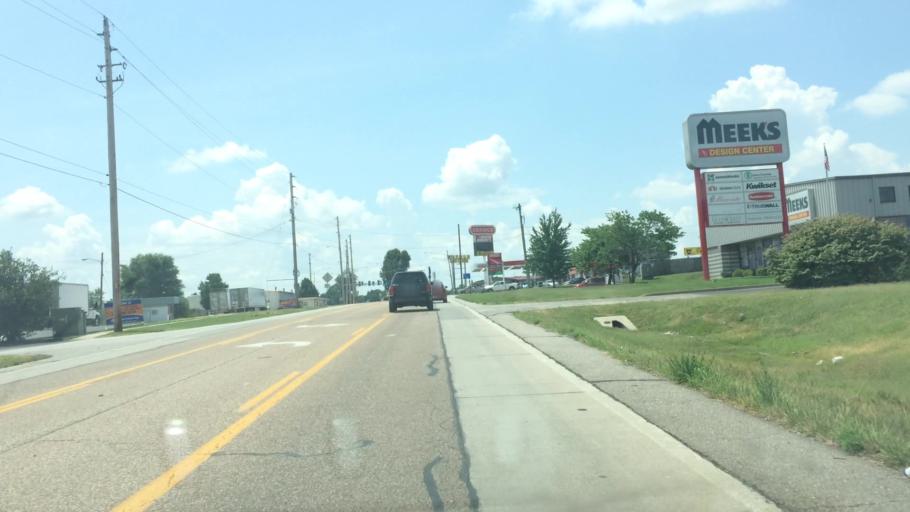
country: US
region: Missouri
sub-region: Greene County
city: Springfield
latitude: 37.2564
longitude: -93.2651
